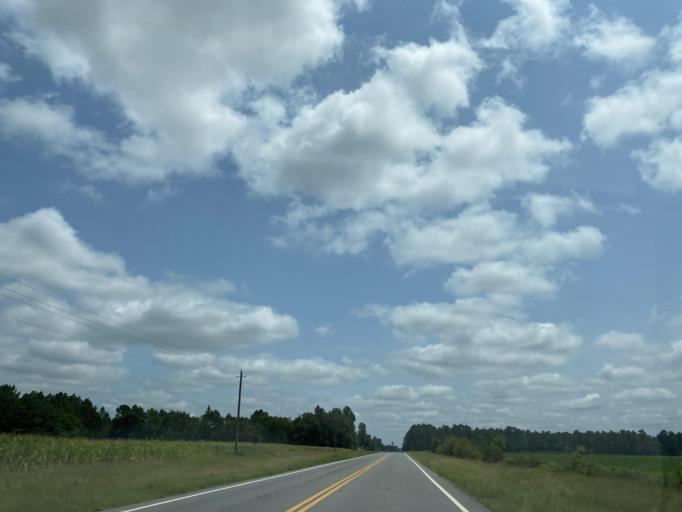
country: US
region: Georgia
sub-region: Bacon County
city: Alma
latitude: 31.6829
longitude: -82.4997
